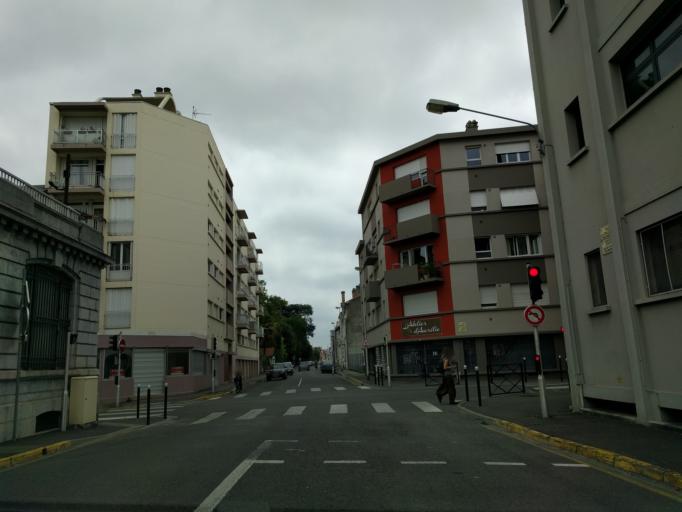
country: FR
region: Midi-Pyrenees
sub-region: Departement des Hautes-Pyrenees
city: Tarbes
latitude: 43.2357
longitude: 0.0738
